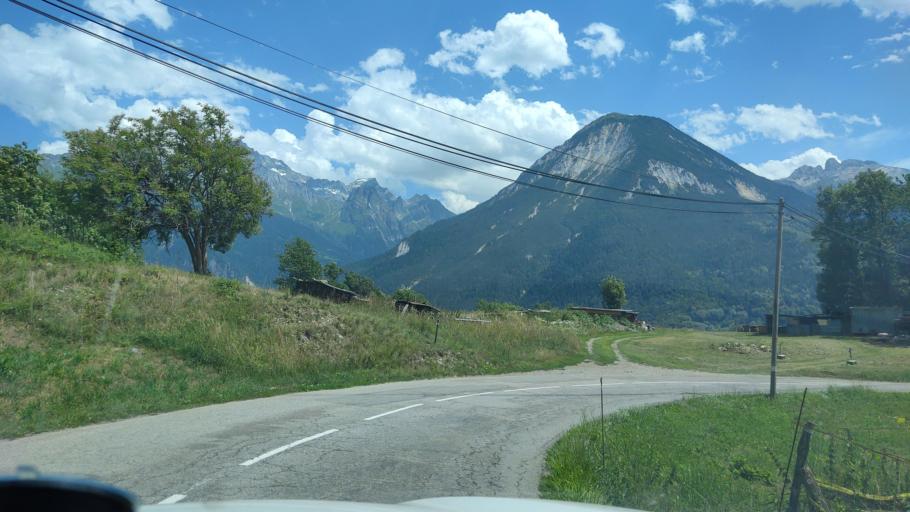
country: FR
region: Rhone-Alpes
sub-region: Departement de la Savoie
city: Bozel
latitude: 45.4482
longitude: 6.6411
